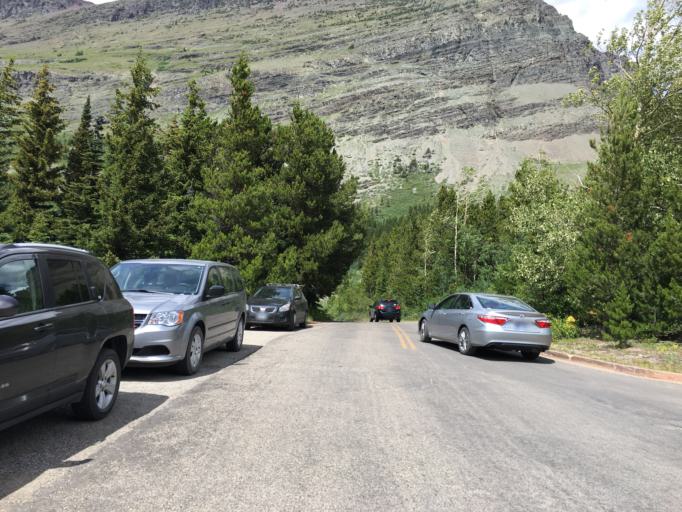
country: CA
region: Alberta
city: Cardston
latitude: 48.7973
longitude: -113.6560
